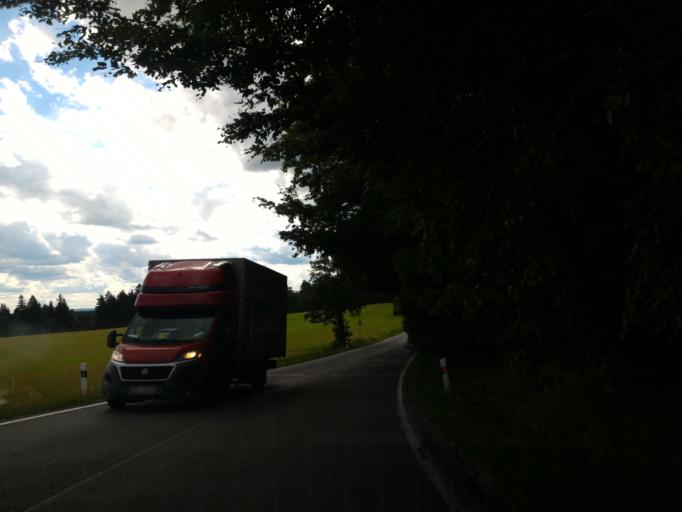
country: CZ
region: Vysocina
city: Bohdalov
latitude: 49.4604
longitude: 15.8224
